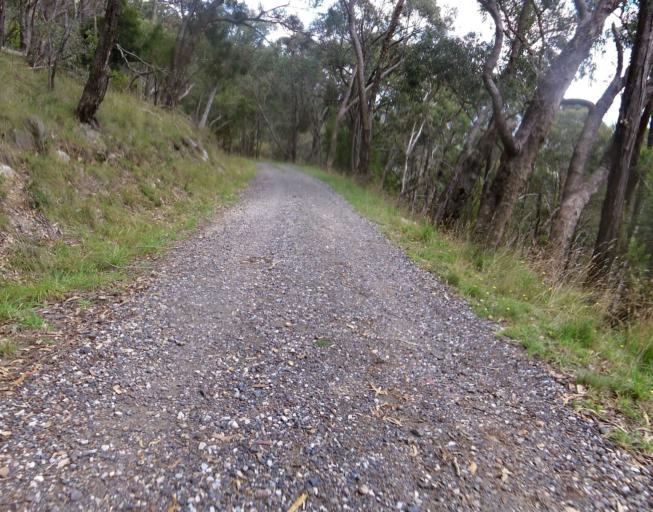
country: AU
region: Victoria
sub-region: Yarra Ranges
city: Montrose
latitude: -37.8216
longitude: 145.3483
